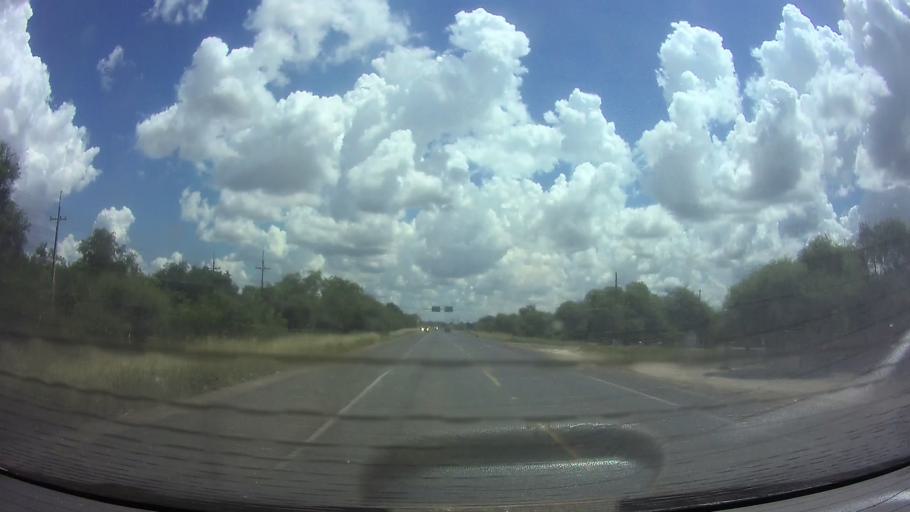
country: PY
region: Central
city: Colonia Mariano Roque Alonso
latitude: -25.1737
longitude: -57.5721
